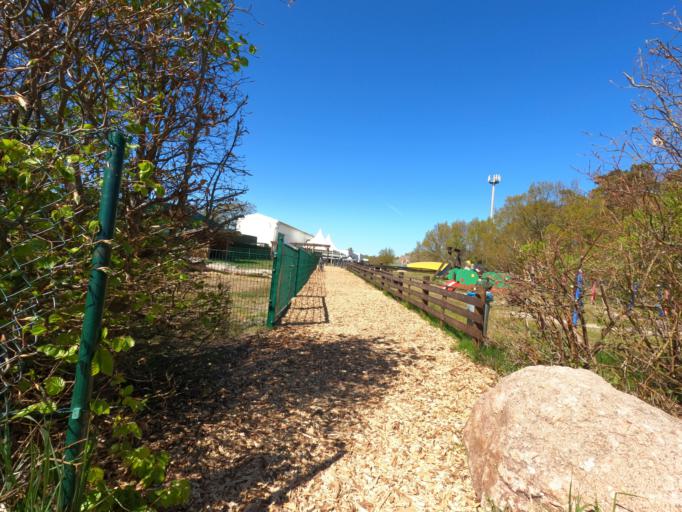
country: DE
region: Mecklenburg-Vorpommern
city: Born
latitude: 54.3844
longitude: 12.5204
